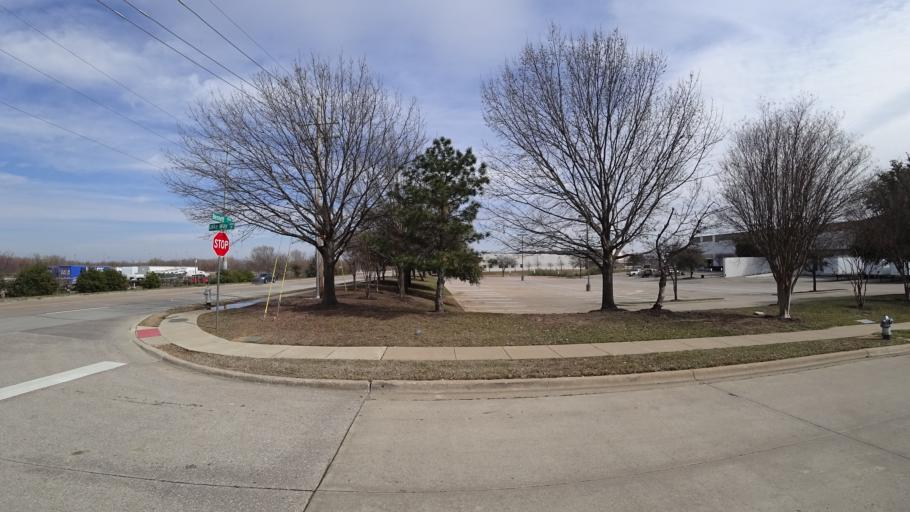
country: US
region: Texas
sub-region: Denton County
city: Lewisville
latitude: 33.0272
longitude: -96.9788
